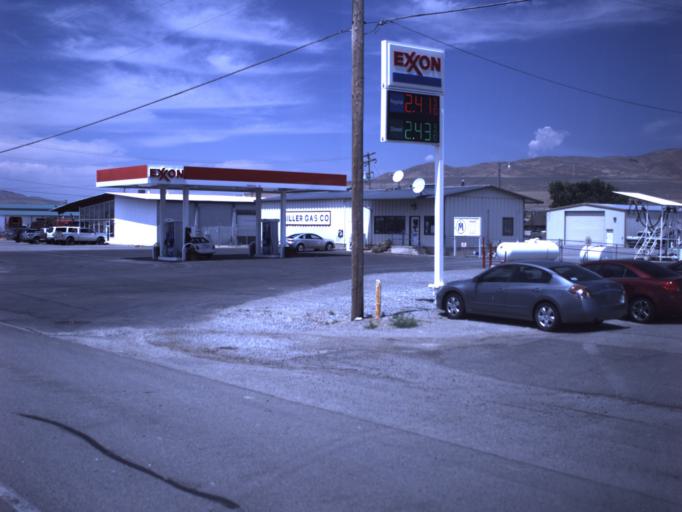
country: US
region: Utah
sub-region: Box Elder County
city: Tremonton
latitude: 41.7112
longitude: -112.1873
